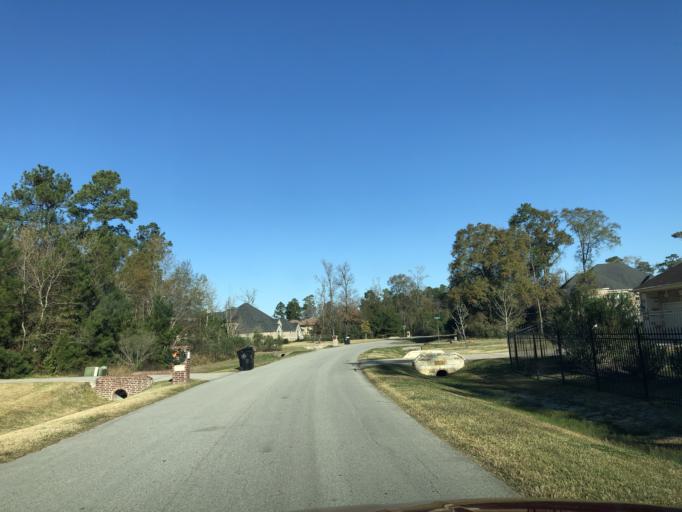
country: US
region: Texas
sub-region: Montgomery County
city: Porter Heights
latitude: 30.0774
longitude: -95.3368
